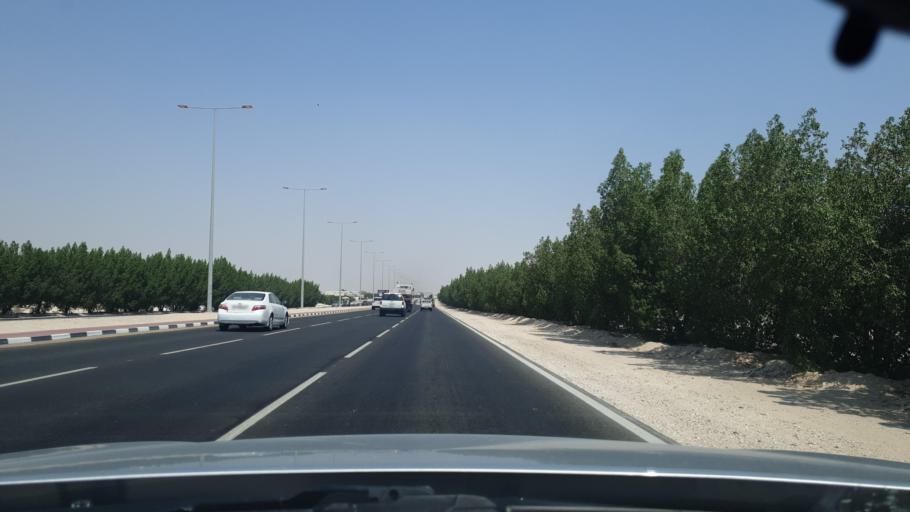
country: QA
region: Al Khawr
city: Al Khawr
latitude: 25.7033
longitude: 51.5042
